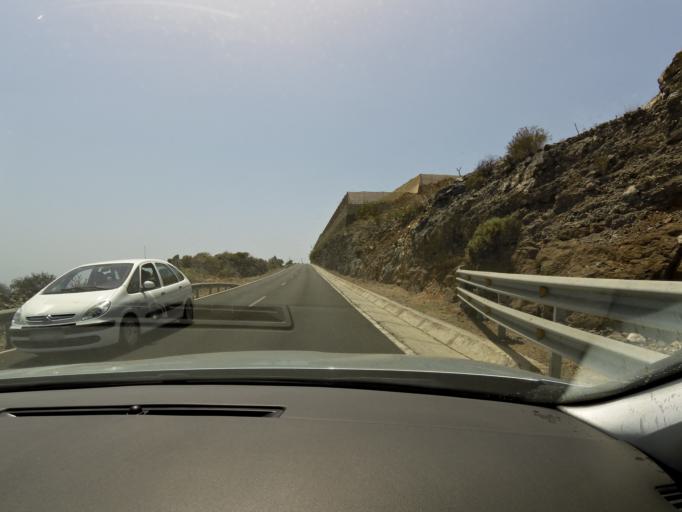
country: ES
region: Canary Islands
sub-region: Provincia de Santa Cruz de Tenerife
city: Guia de Isora
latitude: 28.1594
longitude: -16.7958
